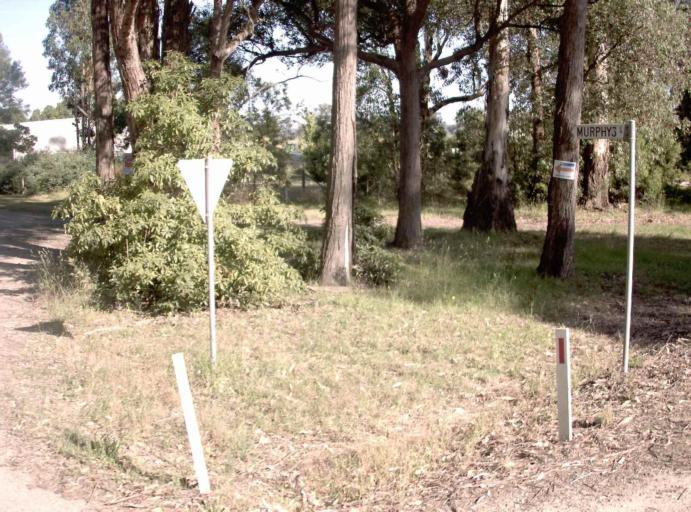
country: AU
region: Victoria
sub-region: East Gippsland
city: Lakes Entrance
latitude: -37.6884
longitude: 148.4689
